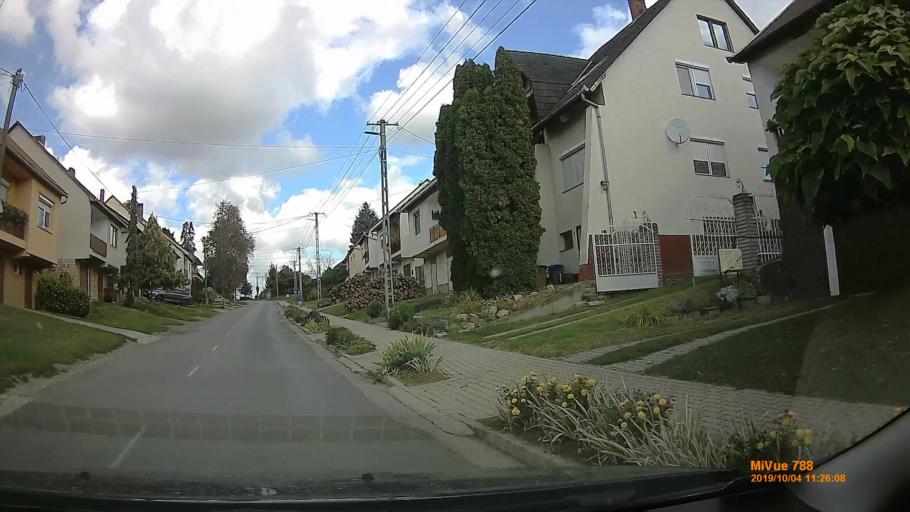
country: HU
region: Somogy
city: Kaposvar
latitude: 46.5075
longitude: 17.8159
